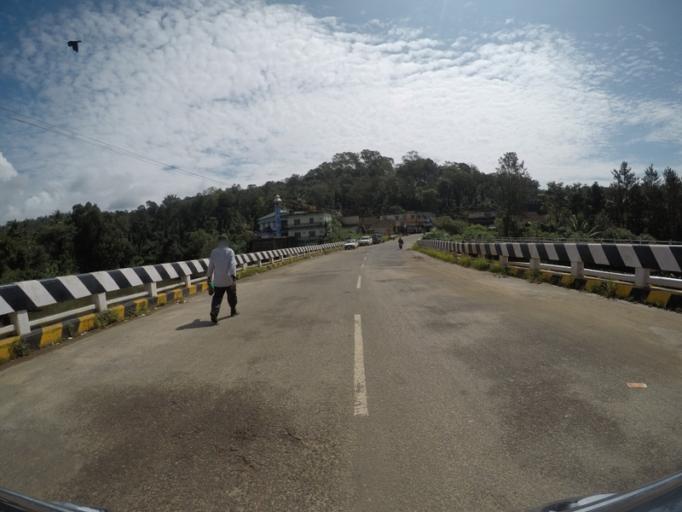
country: IN
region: Karnataka
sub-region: Kodagu
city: Suntikoppa
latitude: 12.5109
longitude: 75.8101
